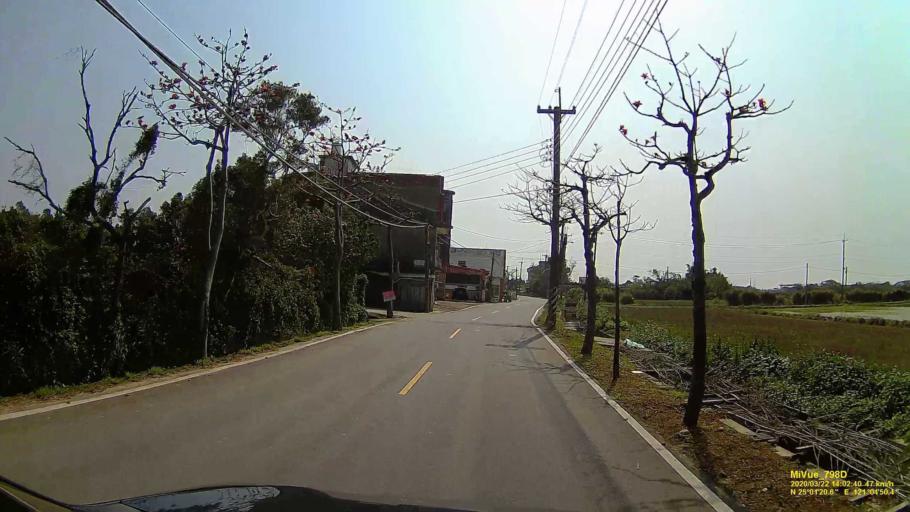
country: TW
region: Taiwan
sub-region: Hsinchu
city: Zhubei
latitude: 25.0222
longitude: 121.0805
